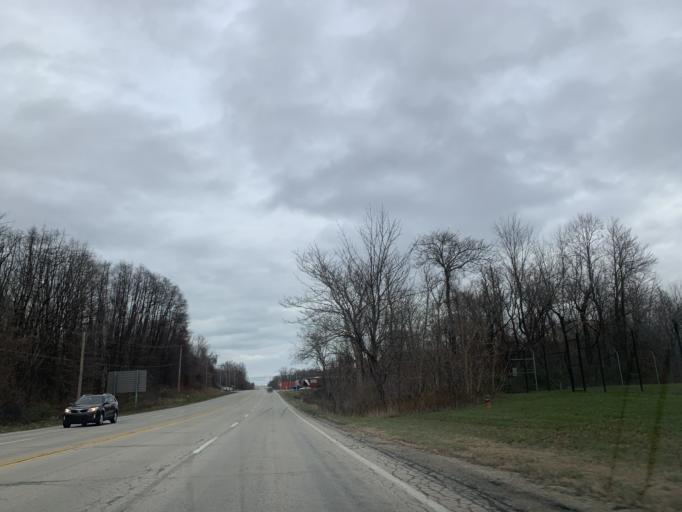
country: US
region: Indiana
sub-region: LaPorte County
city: Trail Creek
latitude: 41.7067
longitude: -86.8259
